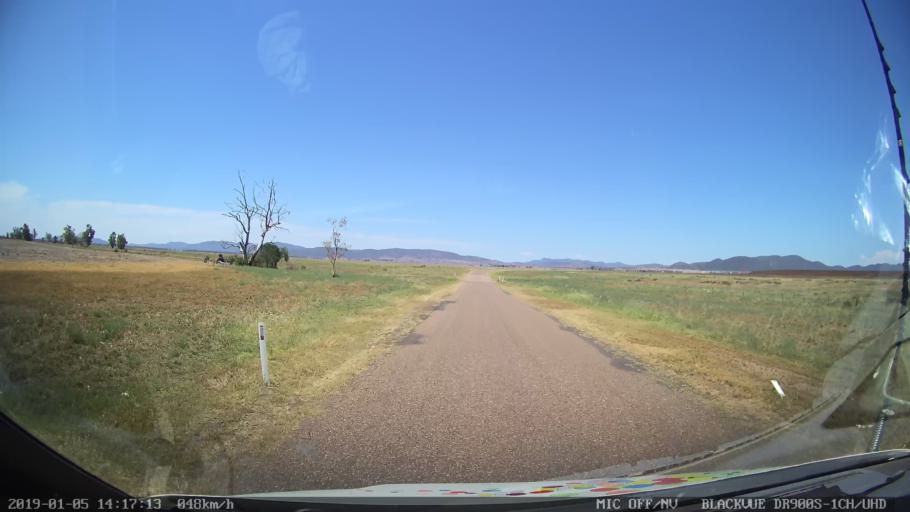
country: AU
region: New South Wales
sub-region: Liverpool Plains
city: Quirindi
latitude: -31.2551
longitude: 150.4755
